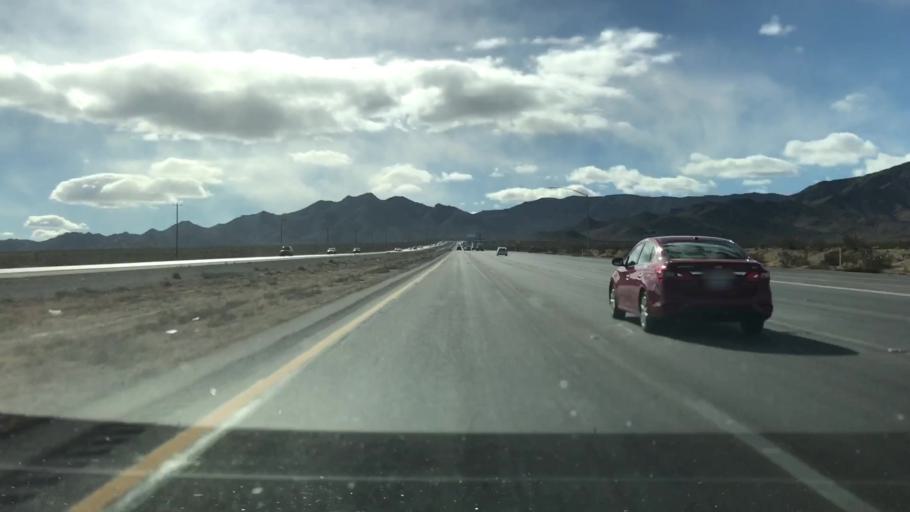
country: US
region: Nevada
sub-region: Clark County
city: Sandy Valley
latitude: 35.4949
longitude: -115.4396
